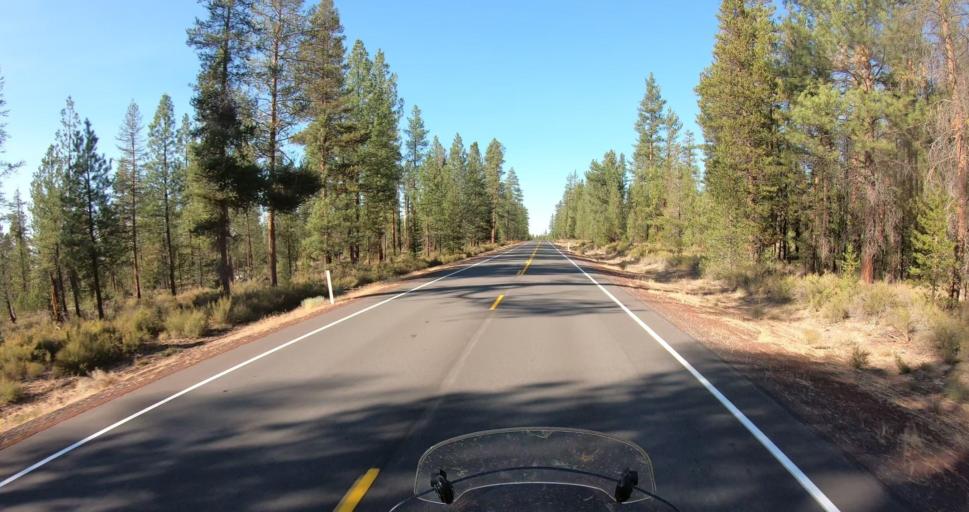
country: US
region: Oregon
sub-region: Deschutes County
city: La Pine
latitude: 43.5062
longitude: -121.4507
